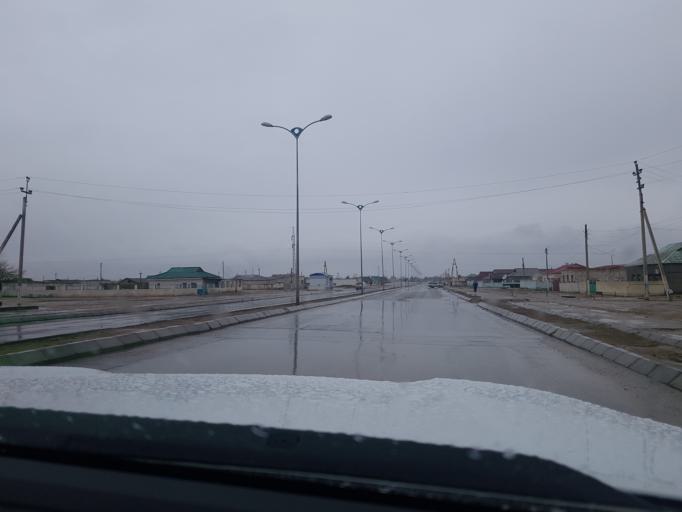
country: TM
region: Balkan
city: Balkanabat
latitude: 39.6334
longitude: 54.2436
